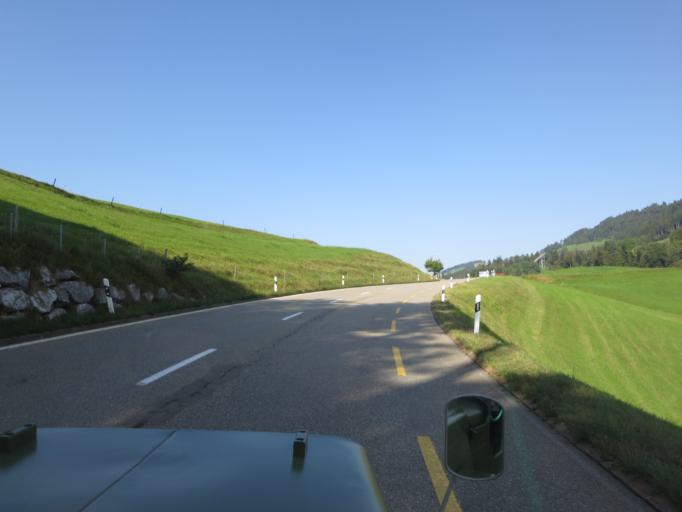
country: CH
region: Zurich
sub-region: Bezirk Hinwil
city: Wald
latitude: 47.3062
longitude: 8.9130
